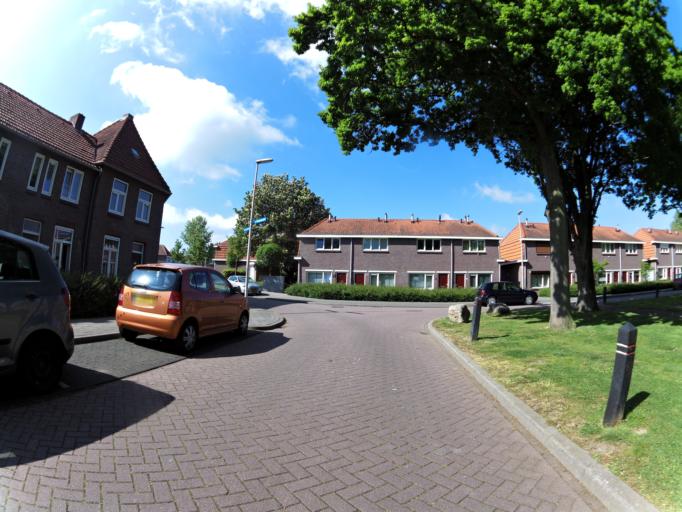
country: NL
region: Limburg
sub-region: Gemeente Heerlen
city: Heerlen
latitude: 50.8850
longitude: 6.0018
